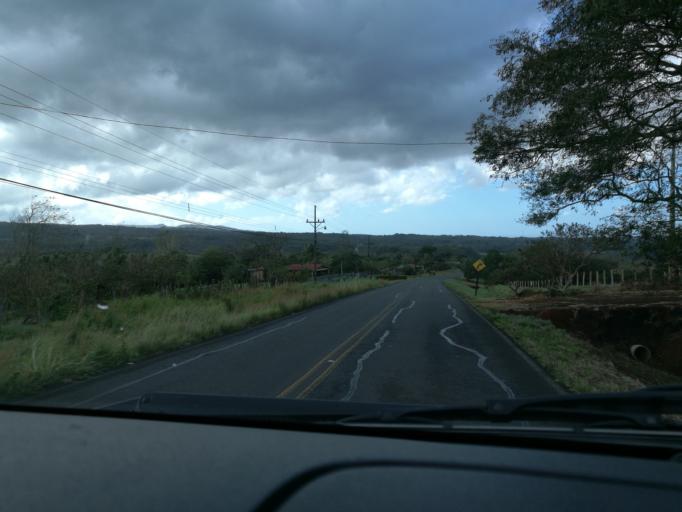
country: CR
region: Alajuela
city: Bijagua
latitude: 10.6678
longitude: -85.0900
